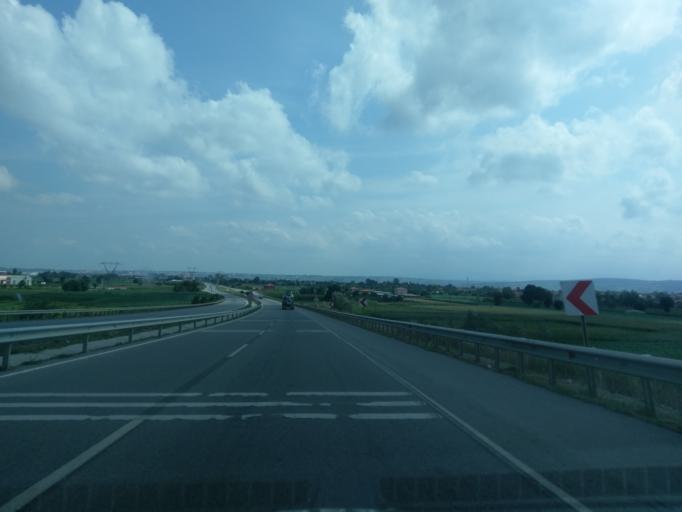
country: TR
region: Samsun
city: Bafra
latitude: 41.5800
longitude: 35.8466
